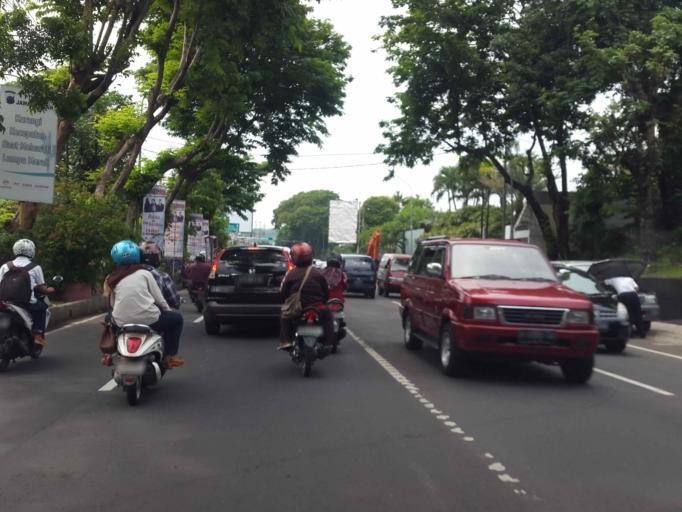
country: ID
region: Central Java
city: Semarang
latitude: -7.0141
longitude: 110.4178
